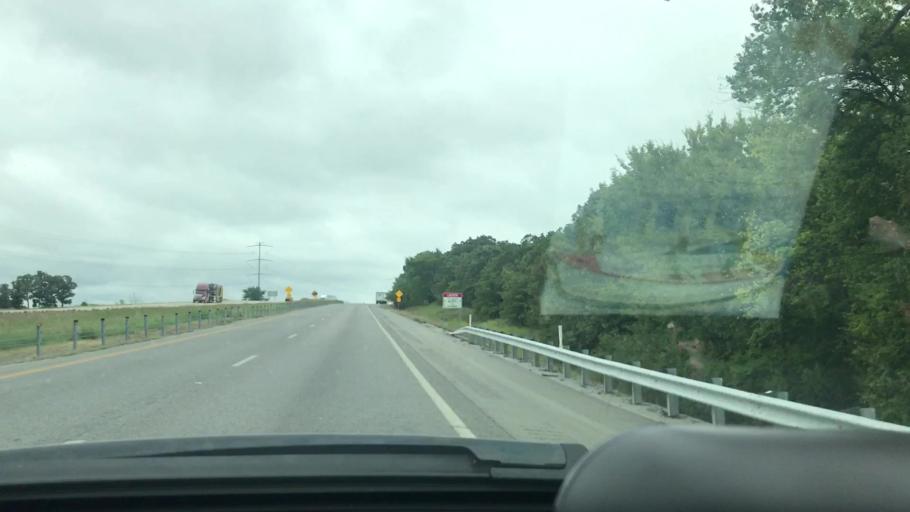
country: US
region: Oklahoma
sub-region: Pittsburg County
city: McAlester
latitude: 34.6735
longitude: -95.9355
